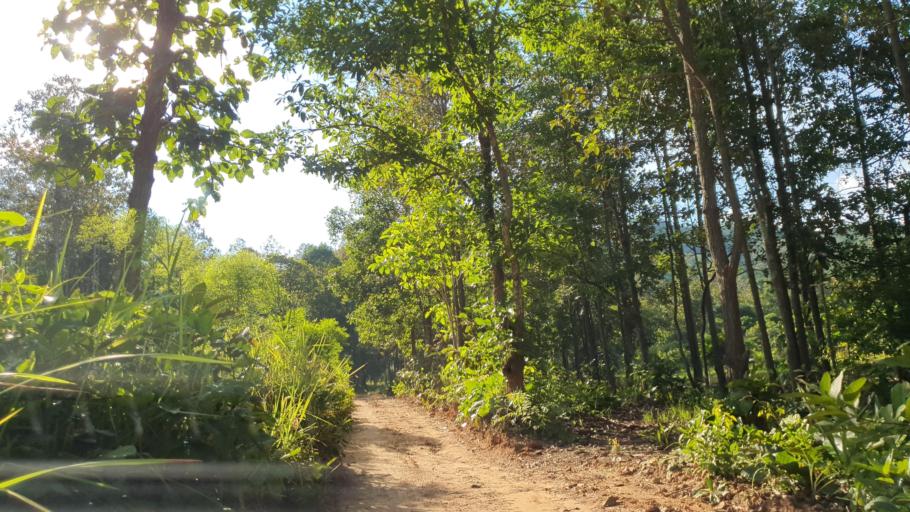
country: TH
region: Chiang Mai
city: Hang Dong
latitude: 18.7234
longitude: 98.8503
